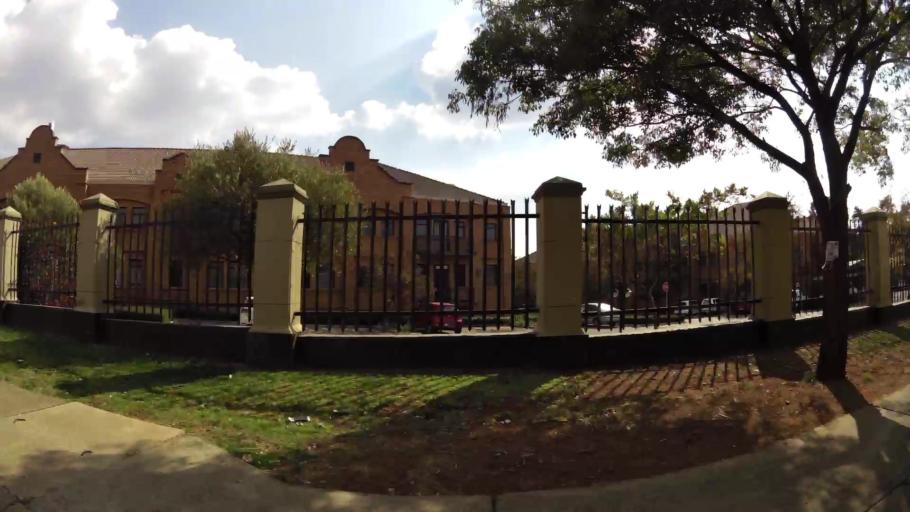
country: ZA
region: Gauteng
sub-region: City of Tshwane Metropolitan Municipality
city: Pretoria
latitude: -25.8003
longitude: 28.3255
